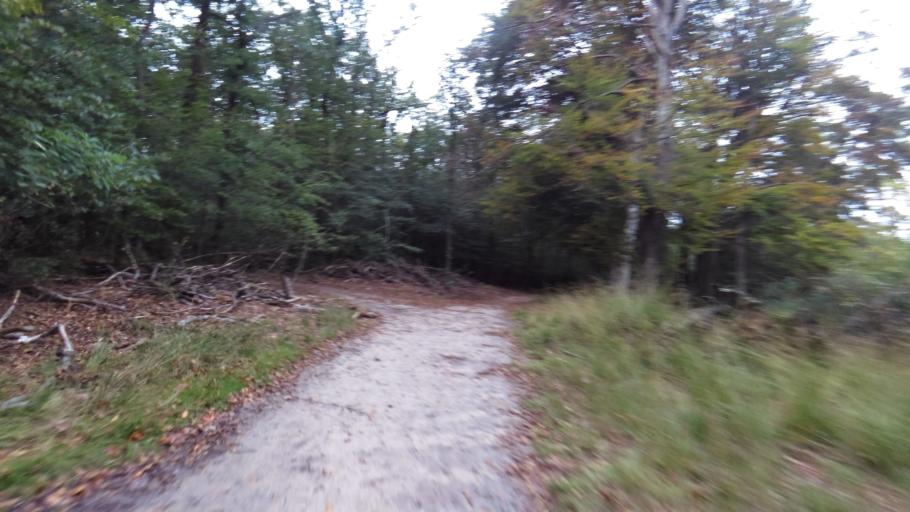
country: NL
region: Gelderland
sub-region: Gemeente Apeldoorn
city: Beekbergen
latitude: 52.1736
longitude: 5.8546
